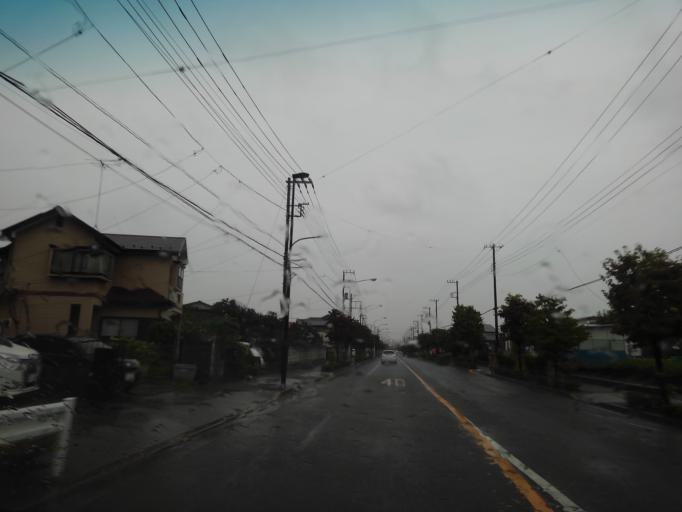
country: JP
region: Tokyo
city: Fussa
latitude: 35.7930
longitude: 139.3506
